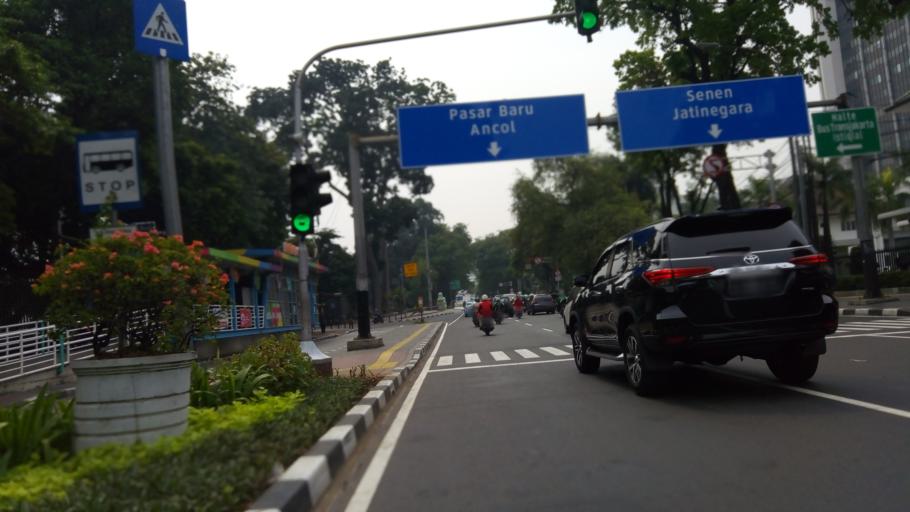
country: ID
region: Jakarta Raya
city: Jakarta
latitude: -6.1723
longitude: 106.8307
